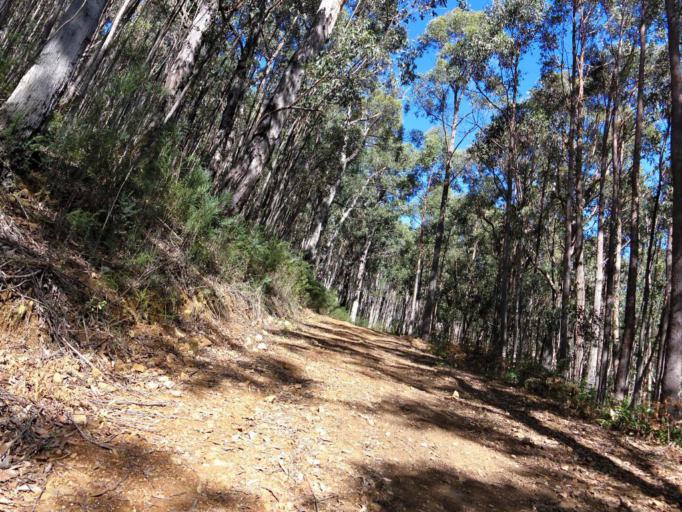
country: AU
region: Victoria
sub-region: Yarra Ranges
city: Millgrove
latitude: -37.7648
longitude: 145.6650
